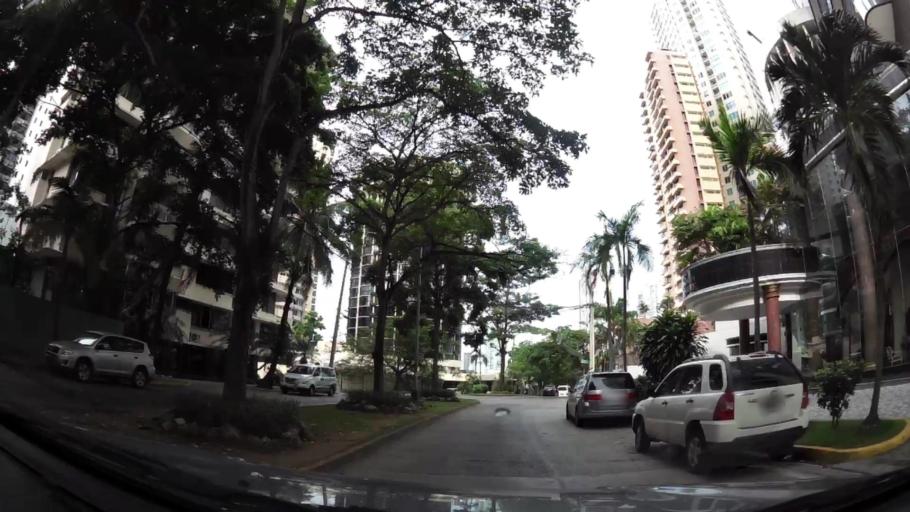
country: PA
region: Panama
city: Panama
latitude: 8.9736
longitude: -79.5154
